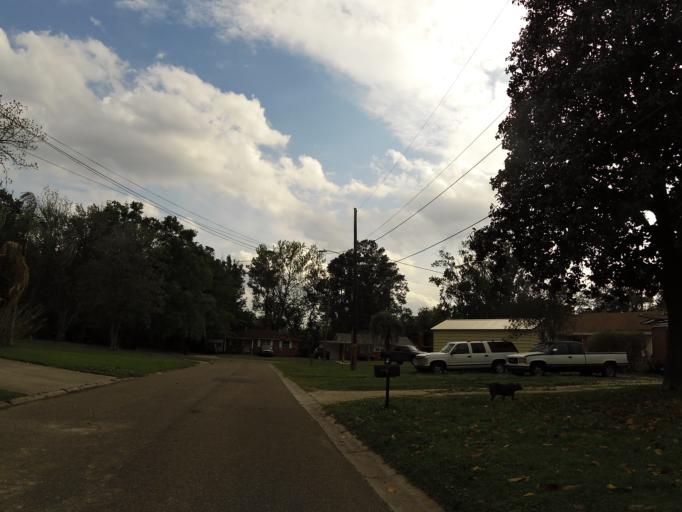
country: US
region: Florida
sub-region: Duval County
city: Jacksonville
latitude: 30.2967
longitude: -81.7322
